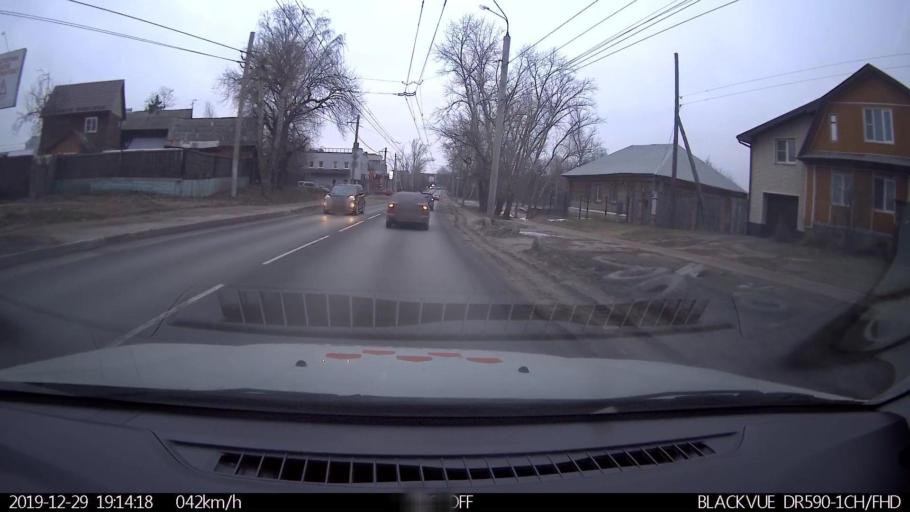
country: RU
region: Nizjnij Novgorod
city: Neklyudovo
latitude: 56.3664
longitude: 43.8469
